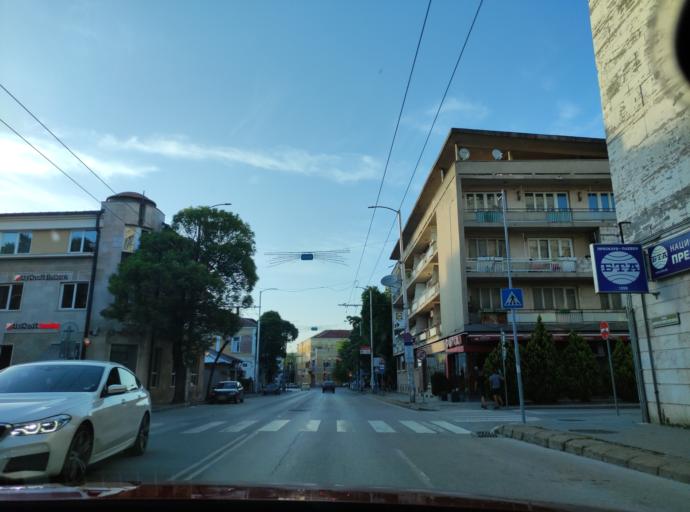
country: BG
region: Pleven
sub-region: Obshtina Pleven
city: Pleven
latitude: 43.4095
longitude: 24.6200
